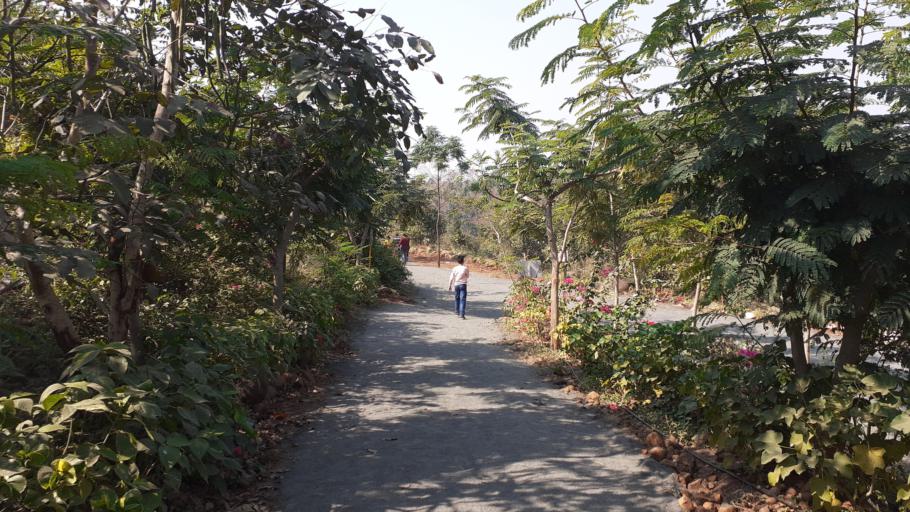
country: IN
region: Maharashtra
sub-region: Nagpur Division
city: Saoner
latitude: 21.4350
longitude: 78.8117
